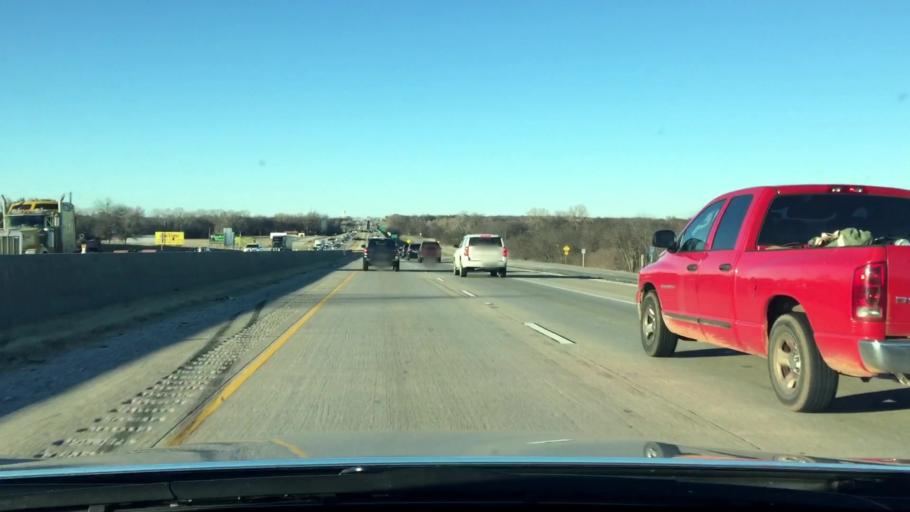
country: US
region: Texas
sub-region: Denton County
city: Sanger
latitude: 33.3279
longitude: -97.1806
